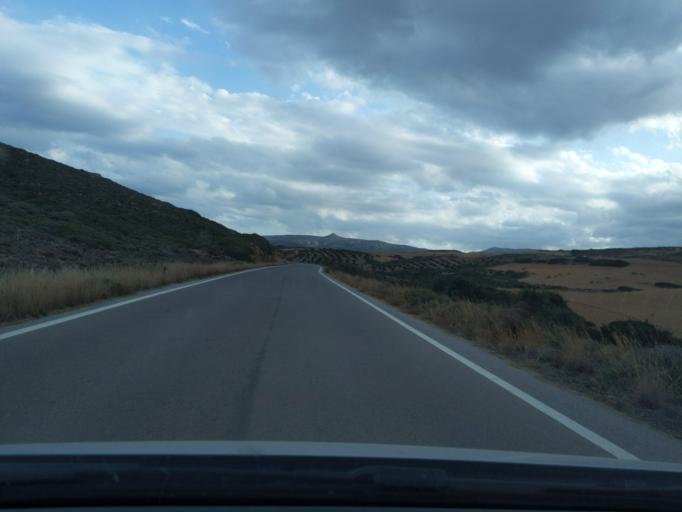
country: GR
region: Crete
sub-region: Nomos Lasithiou
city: Palekastro
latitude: 35.2335
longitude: 26.2522
